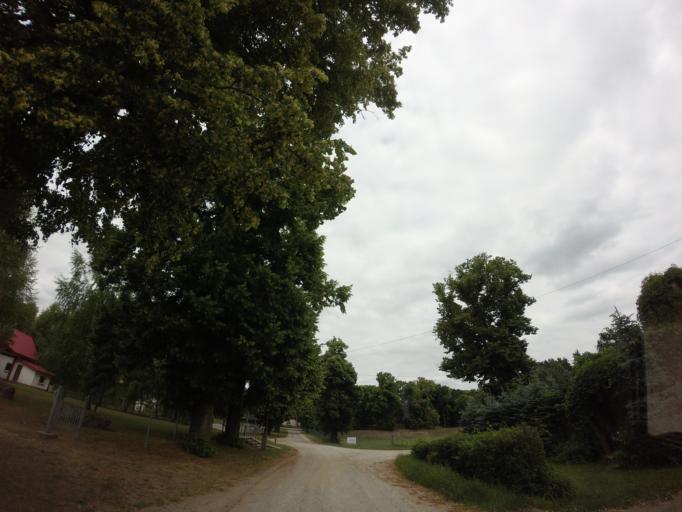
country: PL
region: Lubusz
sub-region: Powiat strzelecko-drezdenecki
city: Stare Kurowo
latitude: 52.9060
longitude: 15.6629
